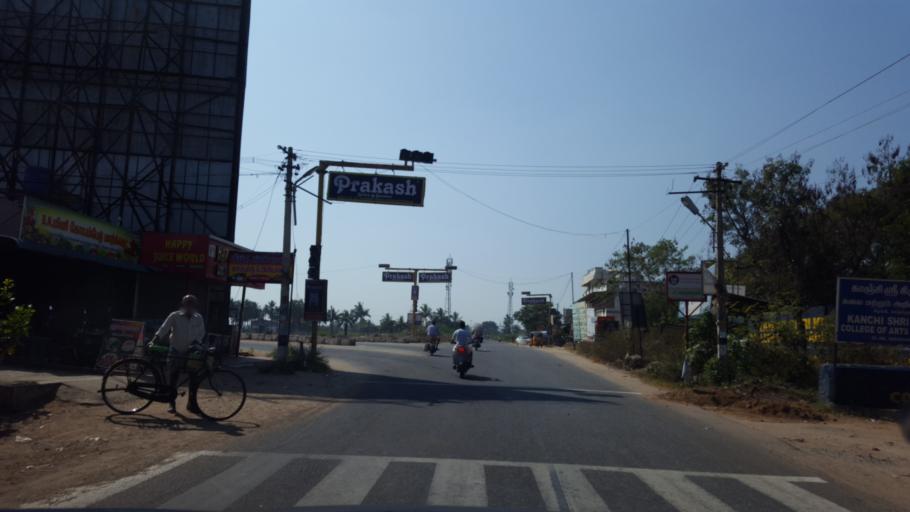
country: IN
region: Tamil Nadu
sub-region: Kancheepuram
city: Kanchipuram
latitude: 12.8676
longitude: 79.6542
